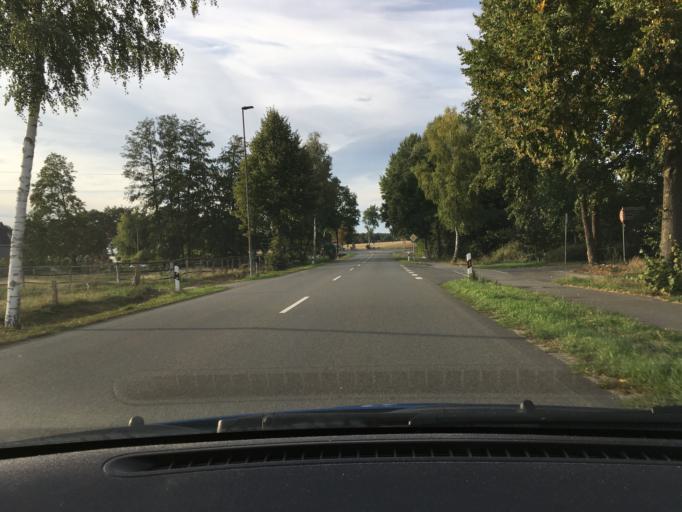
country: DE
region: Lower Saxony
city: Soltau
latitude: 52.9908
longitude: 9.9099
